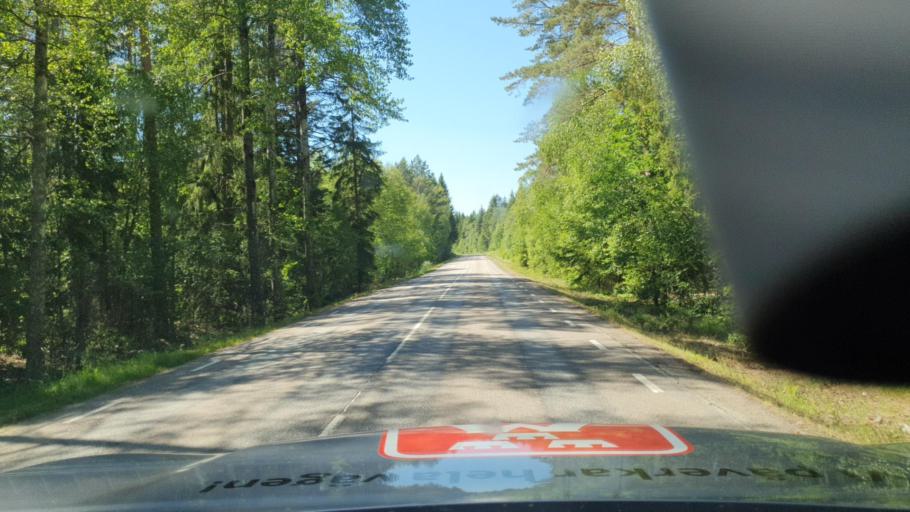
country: SE
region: Kalmar
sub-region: Emmaboda Kommun
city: Emmaboda
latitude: 56.4933
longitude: 15.6898
